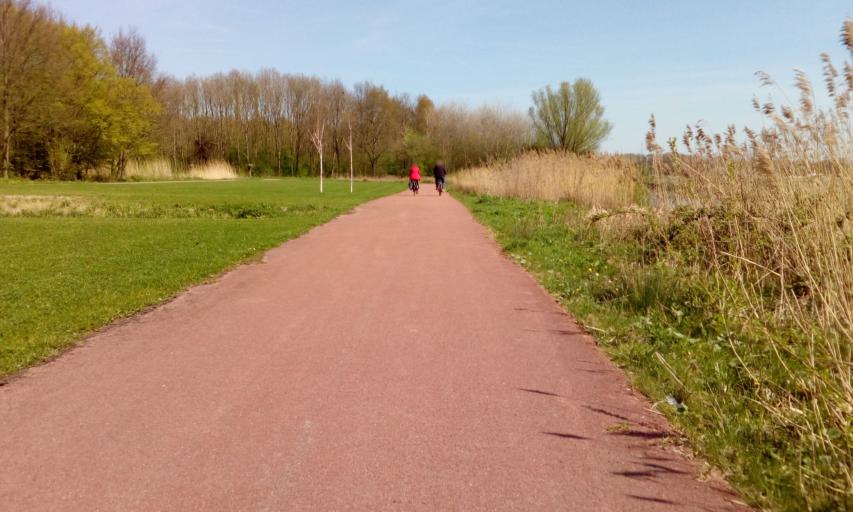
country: NL
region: South Holland
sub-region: Gemeente Rijswijk
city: Rijswijk
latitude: 52.0236
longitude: 4.3344
